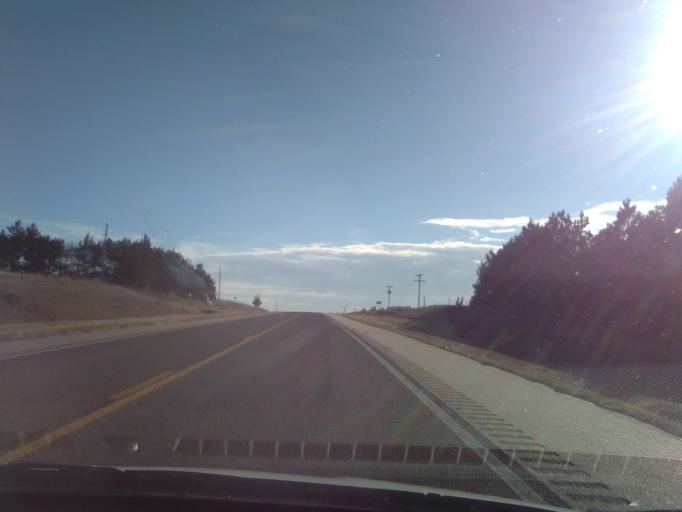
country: US
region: Nebraska
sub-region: Webster County
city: Red Cloud
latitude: 40.3221
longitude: -98.4440
